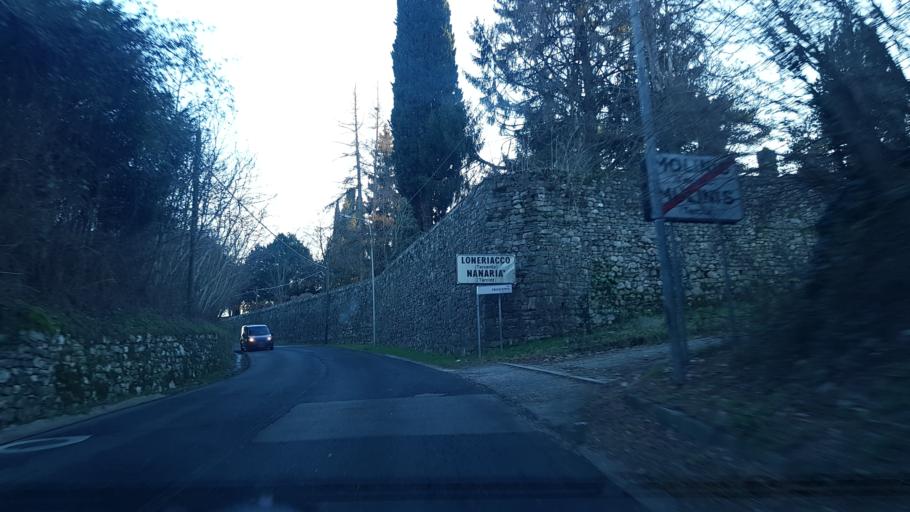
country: IT
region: Friuli Venezia Giulia
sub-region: Provincia di Udine
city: Tarcento
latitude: 46.1964
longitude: 13.2263
